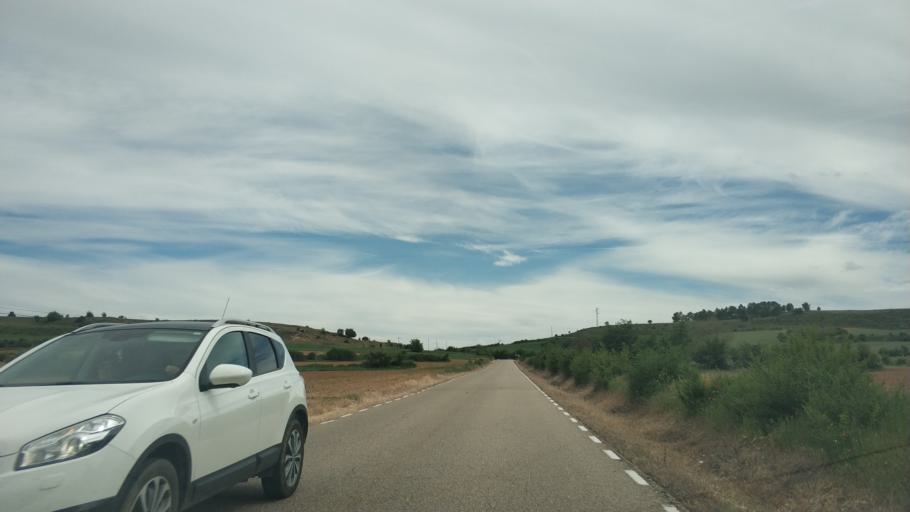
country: ES
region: Castille and Leon
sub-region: Provincia de Soria
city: Berlanga de Duero
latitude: 41.4848
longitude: -2.8657
